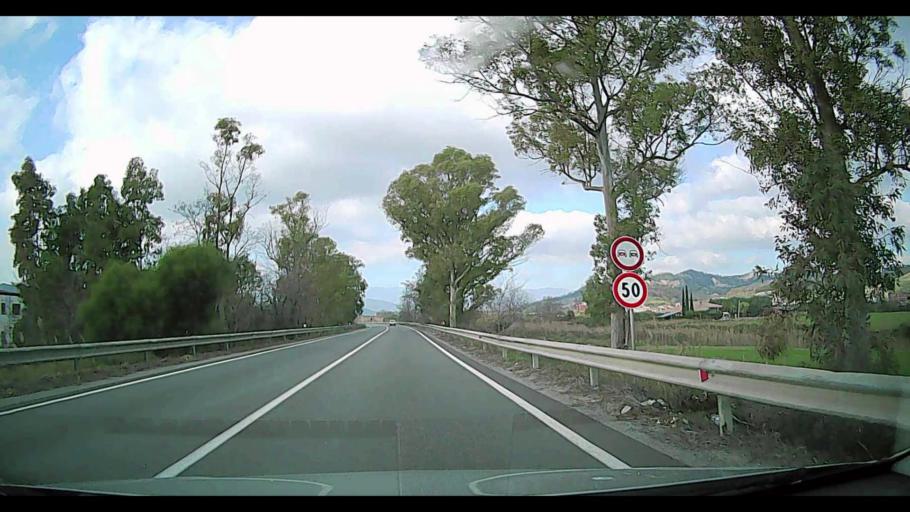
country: IT
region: Calabria
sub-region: Provincia di Crotone
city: Rocca di Neto
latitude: 39.1754
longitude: 17.0054
